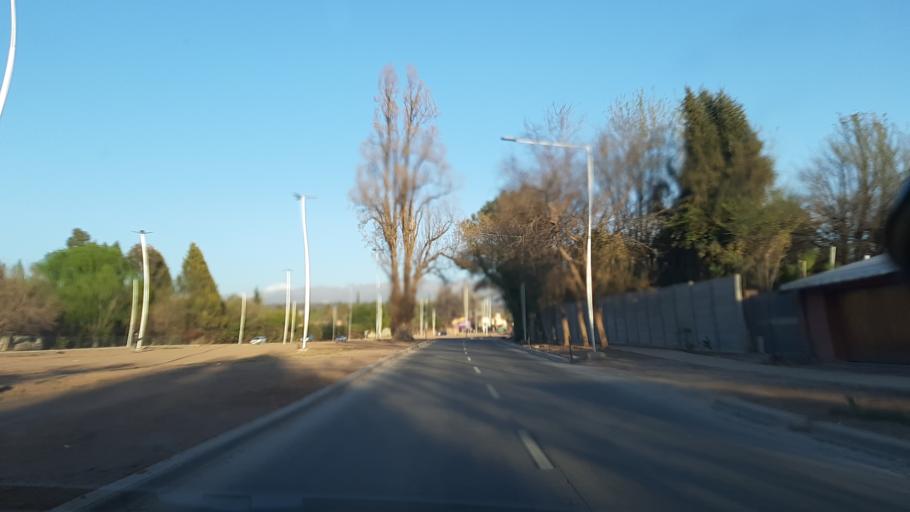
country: AR
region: Mendoza
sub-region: Departamento de Godoy Cruz
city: Godoy Cruz
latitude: -32.9647
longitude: -68.8582
